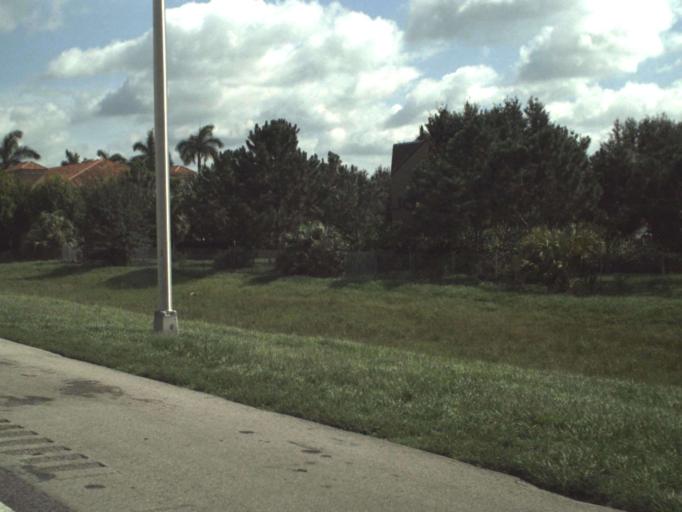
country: US
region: Florida
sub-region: Palm Beach County
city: Limestone Creek
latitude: 26.9228
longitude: -80.1467
